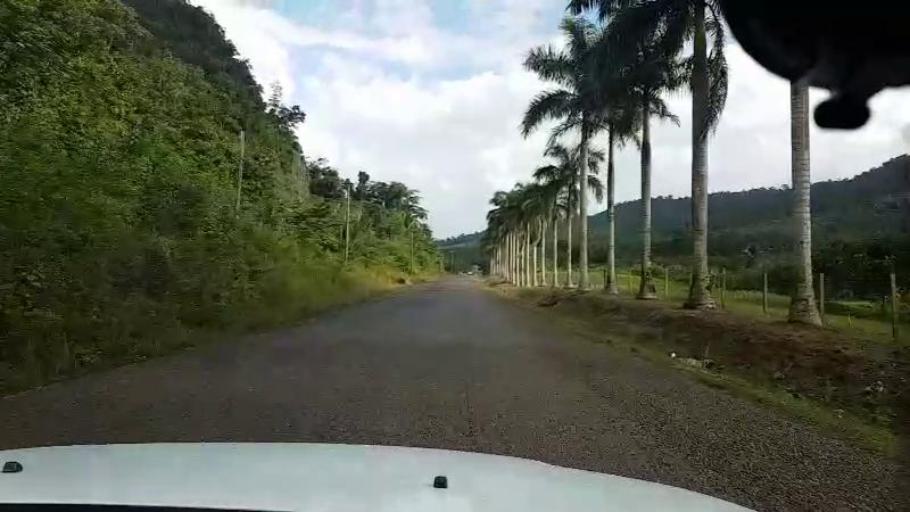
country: BZ
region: Cayo
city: Belmopan
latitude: 17.0909
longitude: -88.6235
